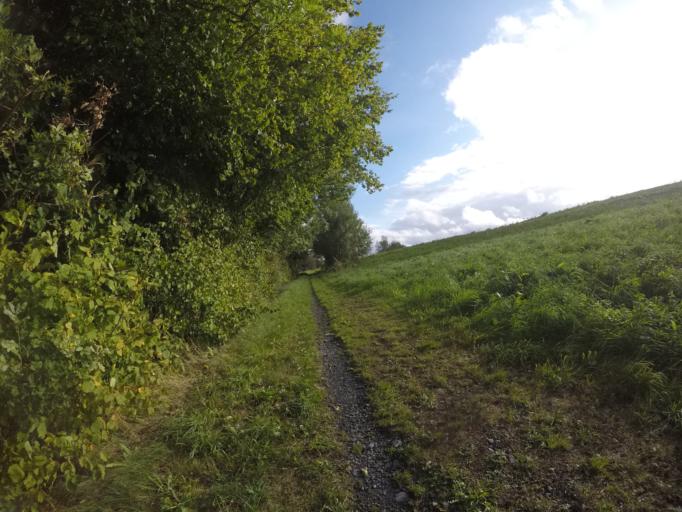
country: BE
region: Wallonia
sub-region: Province du Luxembourg
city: Bastogne
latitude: 49.9500
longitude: 5.6948
